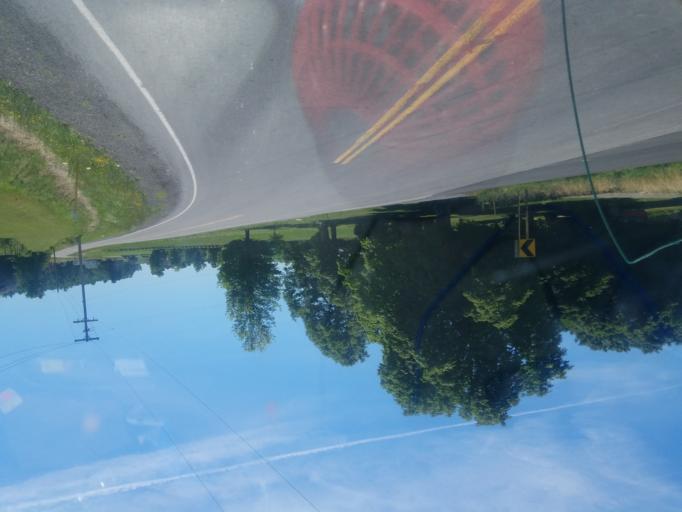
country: US
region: New York
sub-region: Yates County
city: Penn Yan
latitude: 42.6229
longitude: -76.9833
